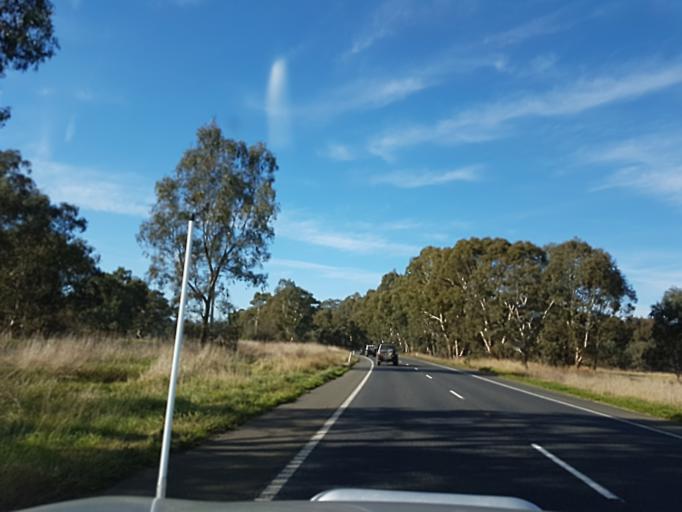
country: AU
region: Victoria
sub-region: Murrindindi
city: Alexandra
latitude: -37.1540
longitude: 145.5723
